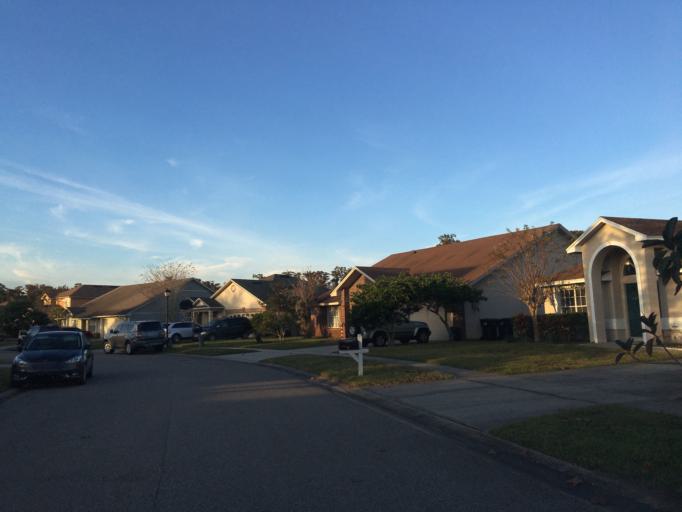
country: US
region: Florida
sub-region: Orange County
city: Azalea Park
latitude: 28.5189
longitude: -81.2758
